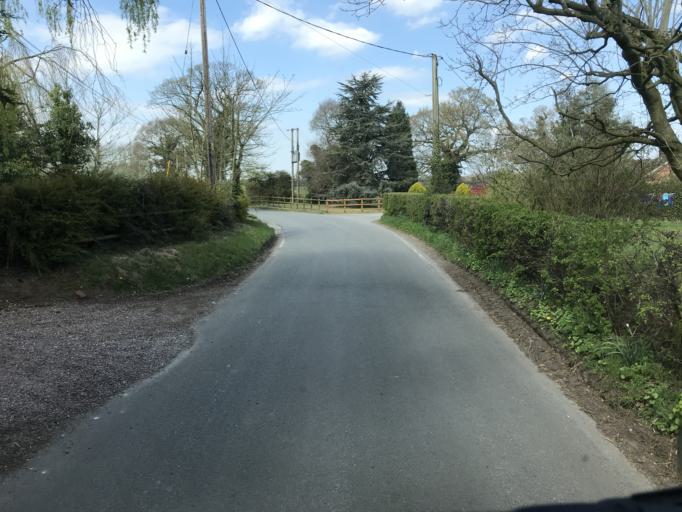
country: GB
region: England
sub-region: Cheshire West and Chester
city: Tarvin
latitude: 53.2075
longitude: -2.7665
